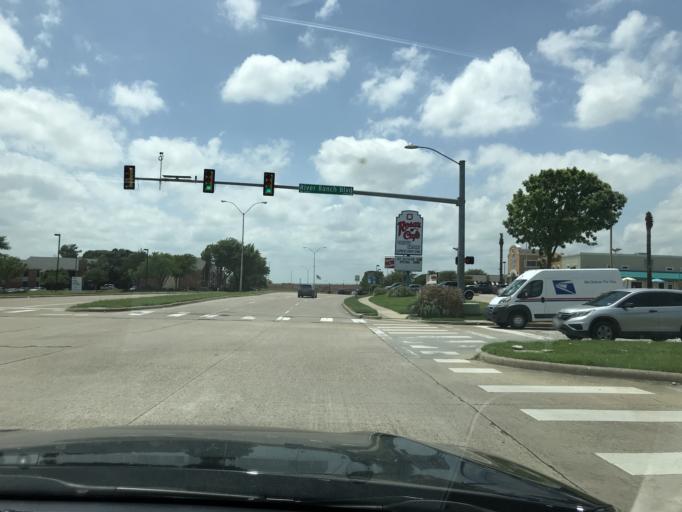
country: US
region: Texas
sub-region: Tarrant County
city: Benbrook
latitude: 32.6767
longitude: -97.4030
